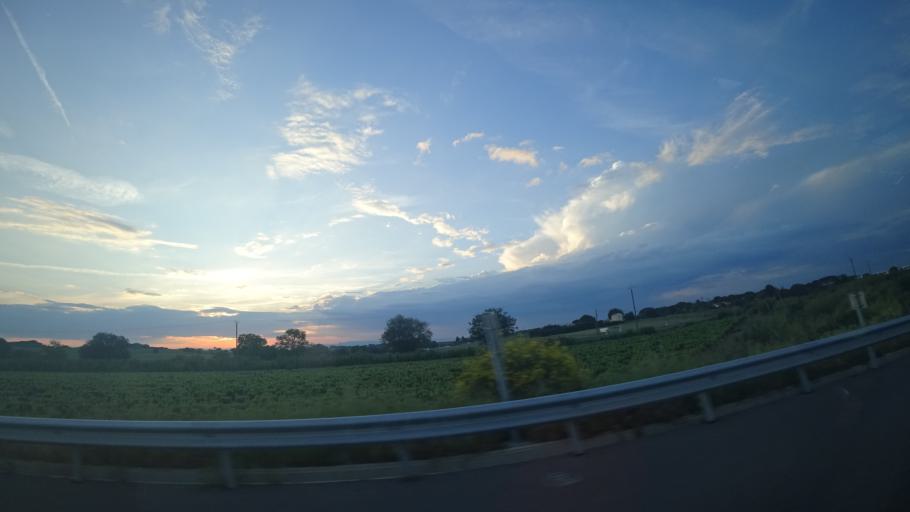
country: FR
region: Languedoc-Roussillon
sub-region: Departement de l'Herault
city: Servian
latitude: 43.3827
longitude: 3.3078
